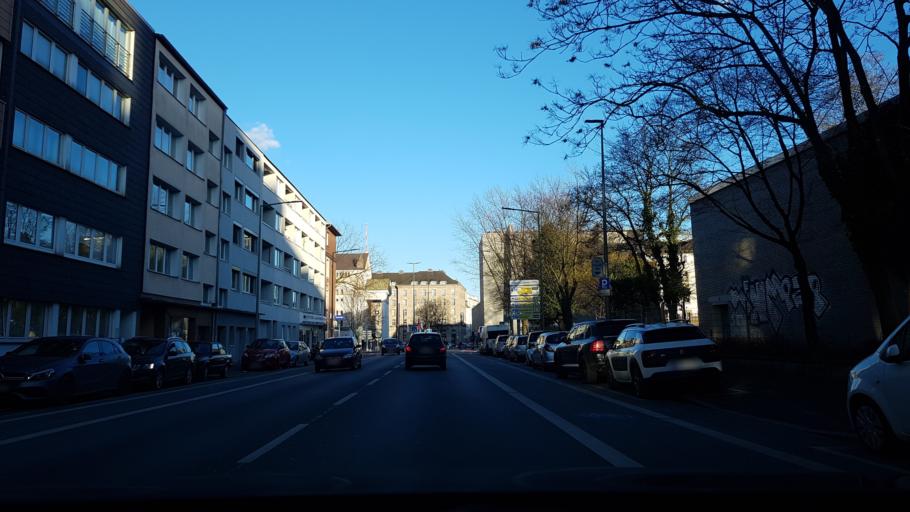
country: DE
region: North Rhine-Westphalia
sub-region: Regierungsbezirk Dusseldorf
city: Duisburg
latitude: 51.4350
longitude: 6.7676
